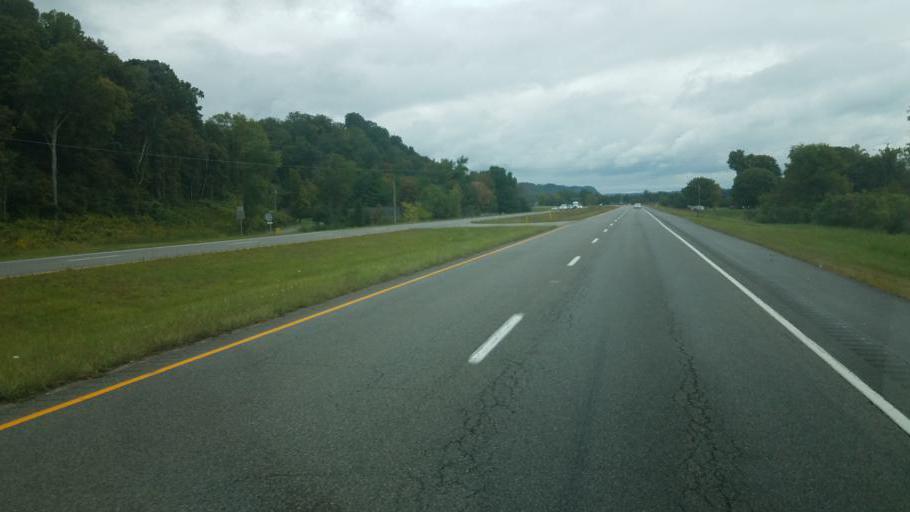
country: US
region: Ohio
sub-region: Scioto County
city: Franklin Furnace
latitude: 38.6622
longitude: -82.8784
